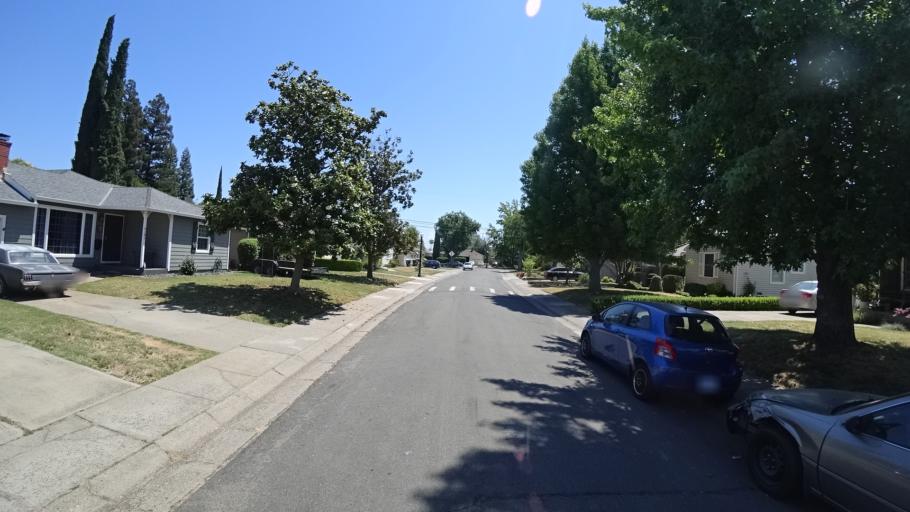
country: US
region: California
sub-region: Sacramento County
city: Parkway
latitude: 38.5387
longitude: -121.4340
